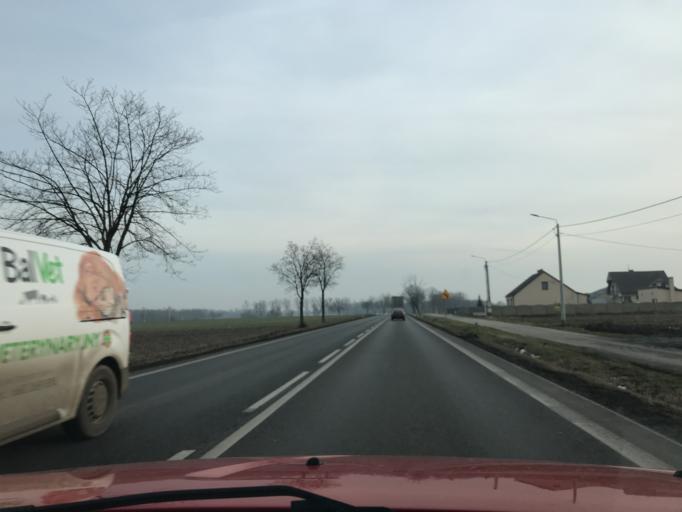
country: PL
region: Greater Poland Voivodeship
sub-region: Powiat ostrowski
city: Nowe Skalmierzyce
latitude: 51.7800
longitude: 18.0150
